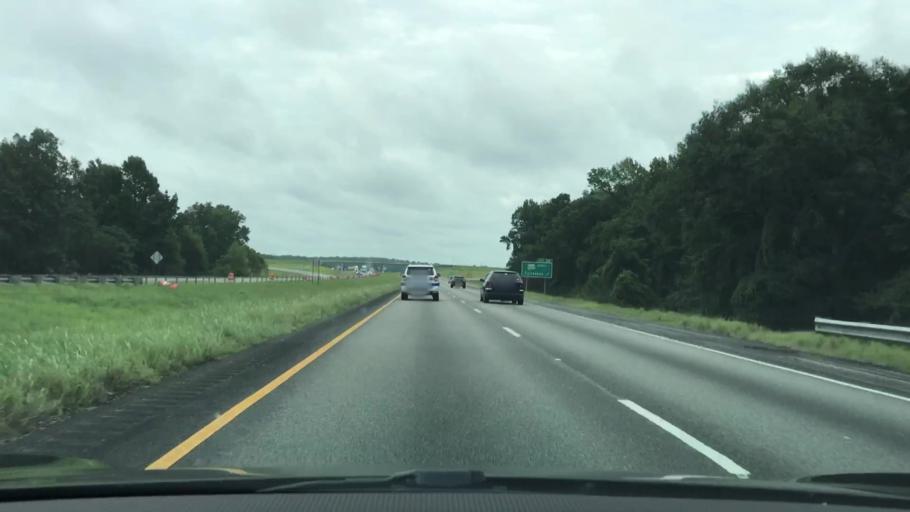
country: US
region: Alabama
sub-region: Elmore County
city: Tallassee
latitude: 32.4270
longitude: -85.9059
